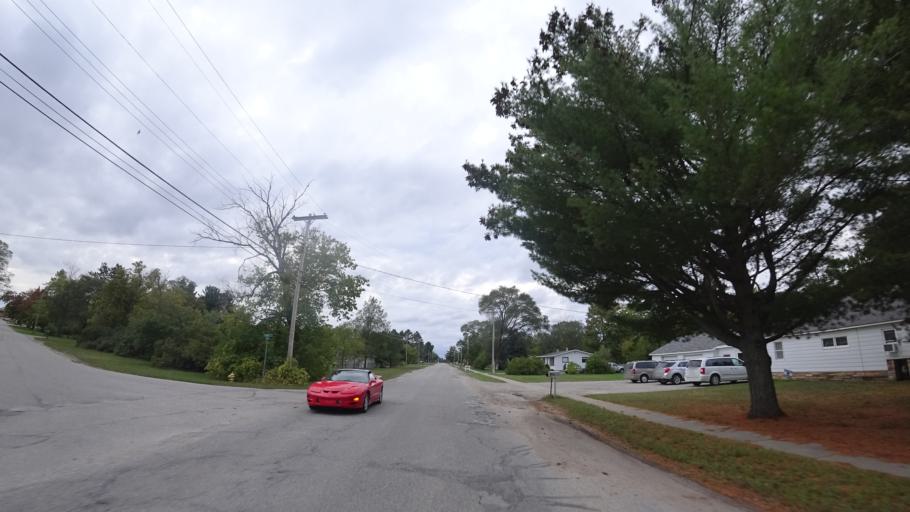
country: US
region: Michigan
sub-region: Kalkaska County
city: Kalkaska
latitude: 44.7355
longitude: -85.1799
